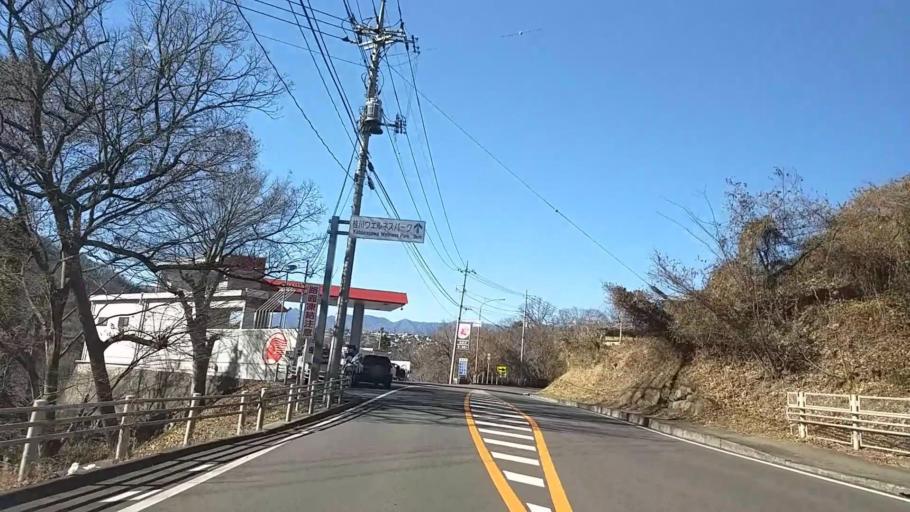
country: JP
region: Yamanashi
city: Otsuki
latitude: 35.6103
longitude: 138.9969
